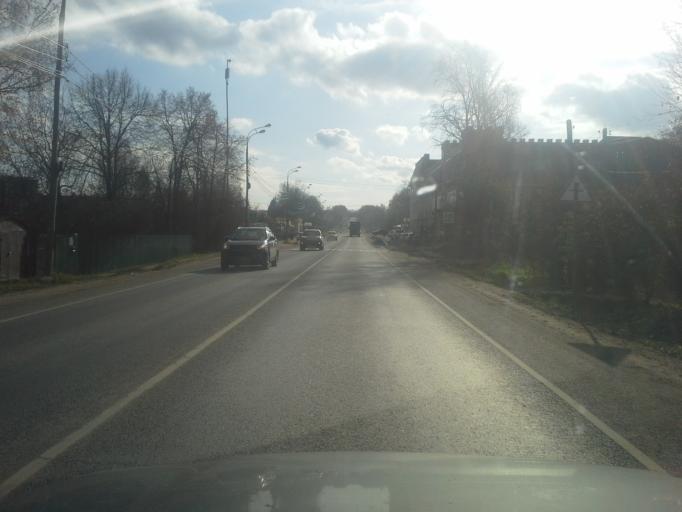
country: RU
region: Moskovskaya
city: Zvenigorod
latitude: 55.6933
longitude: 36.8919
